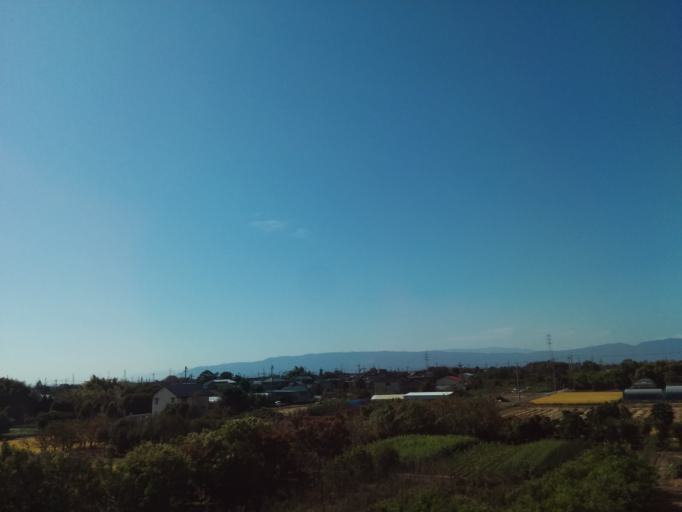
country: JP
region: Aichi
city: Inazawa
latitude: 35.2466
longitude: 136.7714
